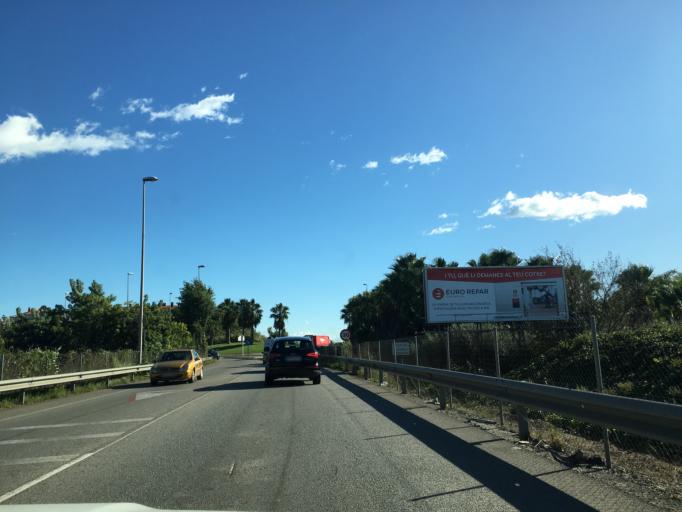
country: ES
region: Catalonia
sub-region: Provincia de Barcelona
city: Sant Feliu de Llobregat
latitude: 41.3685
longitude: 2.0488
